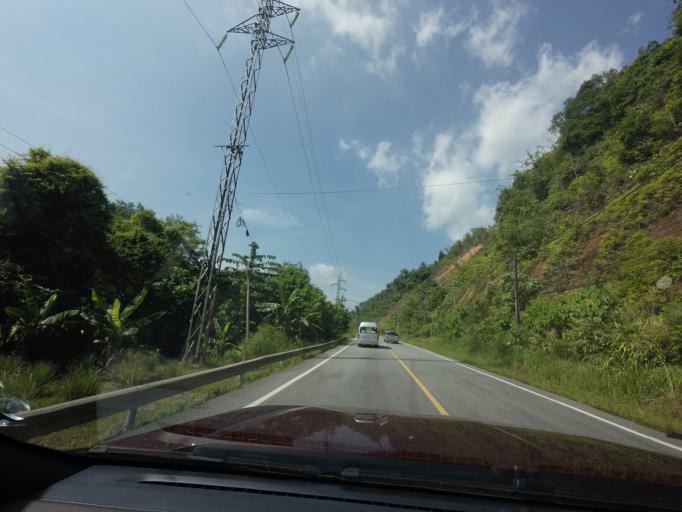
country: TH
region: Yala
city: Betong
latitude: 5.9336
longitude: 101.1857
